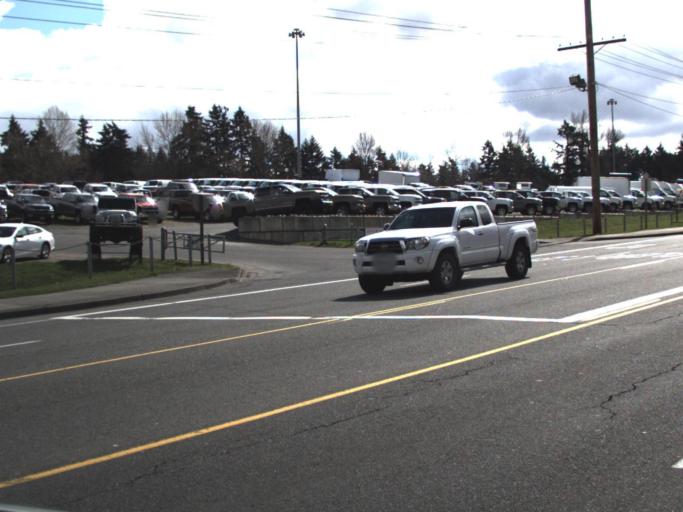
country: US
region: Washington
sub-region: King County
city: Lakeland South
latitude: 47.2810
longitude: -122.3121
